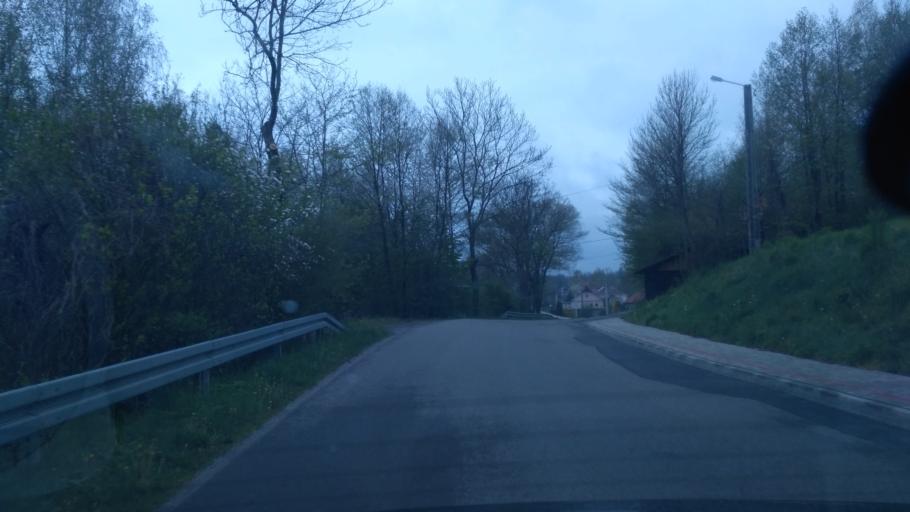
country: PL
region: Subcarpathian Voivodeship
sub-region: Powiat rzeszowski
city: Lecka
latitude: 49.8706
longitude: 22.0512
